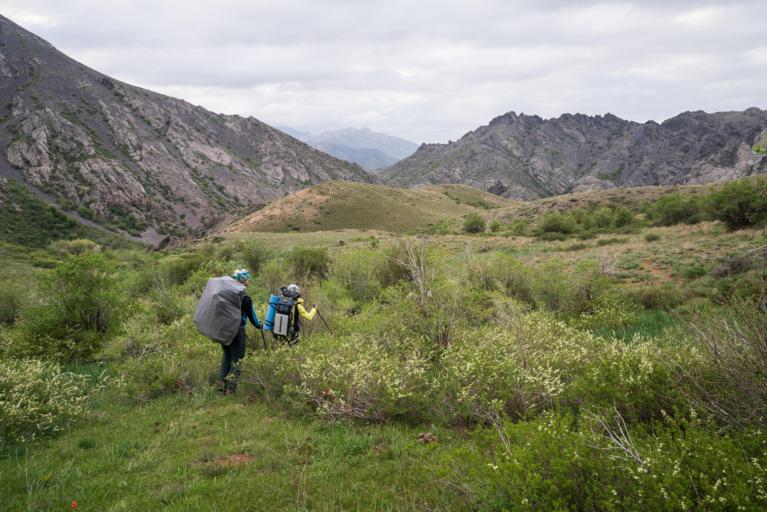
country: KZ
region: Ongtustik Qazaqstan
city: Ashchysay
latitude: 43.6667
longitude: 68.8739
